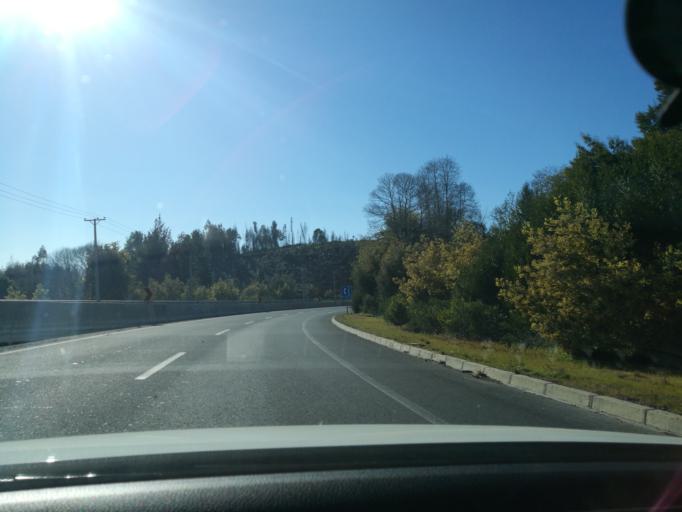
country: CL
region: Biobio
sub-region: Provincia de Concepcion
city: Penco
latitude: -36.8498
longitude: -72.9055
